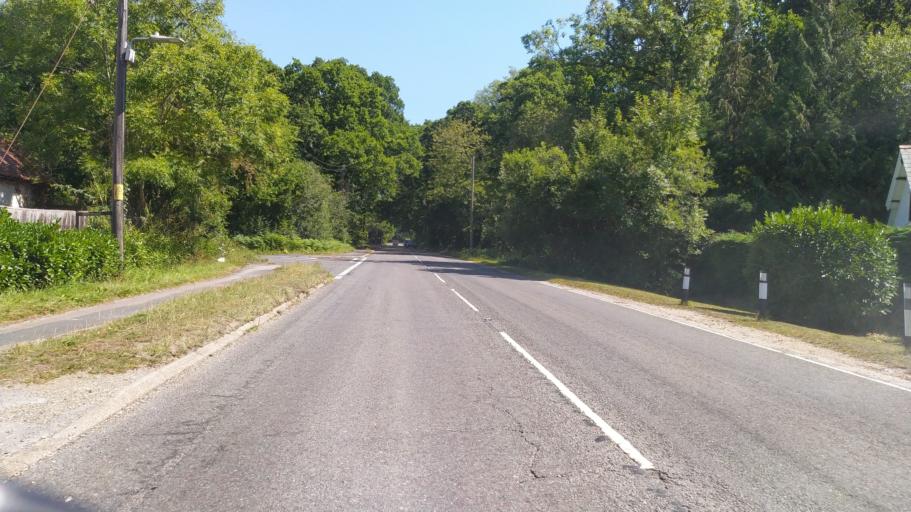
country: GB
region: England
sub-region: Hampshire
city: Cadnam
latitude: 50.9148
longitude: -1.5495
